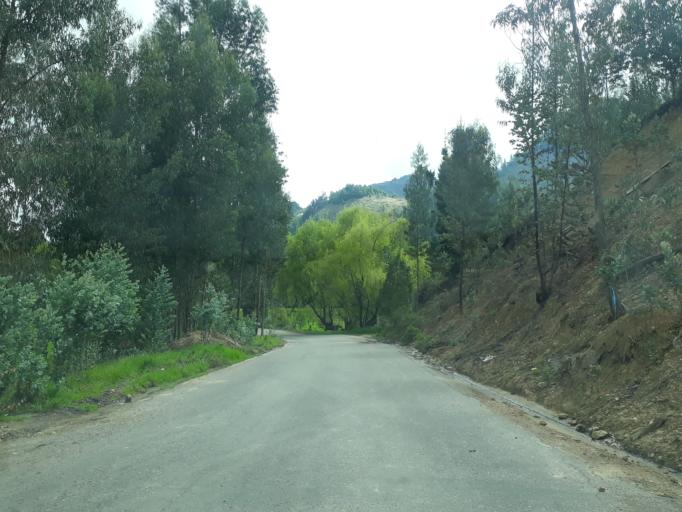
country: CO
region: Cundinamarca
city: Cucunuba
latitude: 5.2416
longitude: -73.7707
